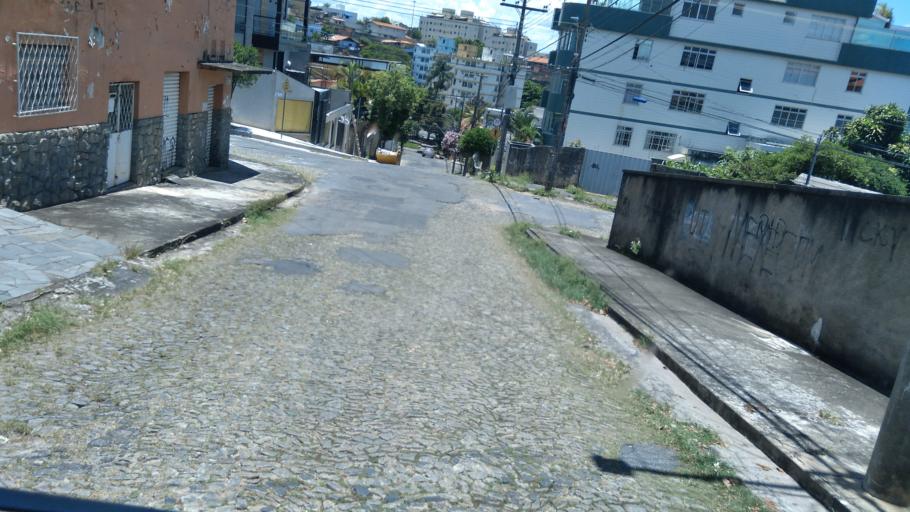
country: BR
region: Minas Gerais
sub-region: Belo Horizonte
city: Belo Horizonte
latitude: -19.9175
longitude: -43.9907
